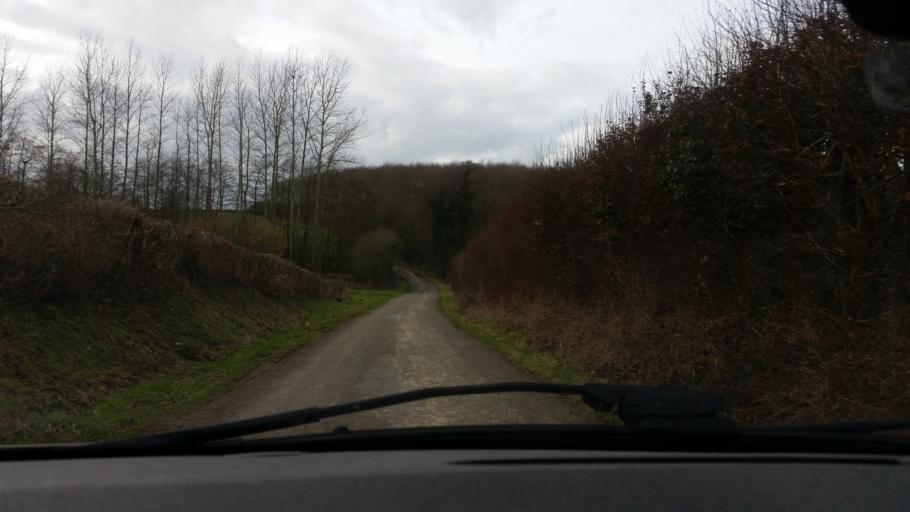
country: FR
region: Nord-Pas-de-Calais
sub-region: Departement du Nord
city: Jeumont
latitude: 50.2394
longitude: 4.1326
